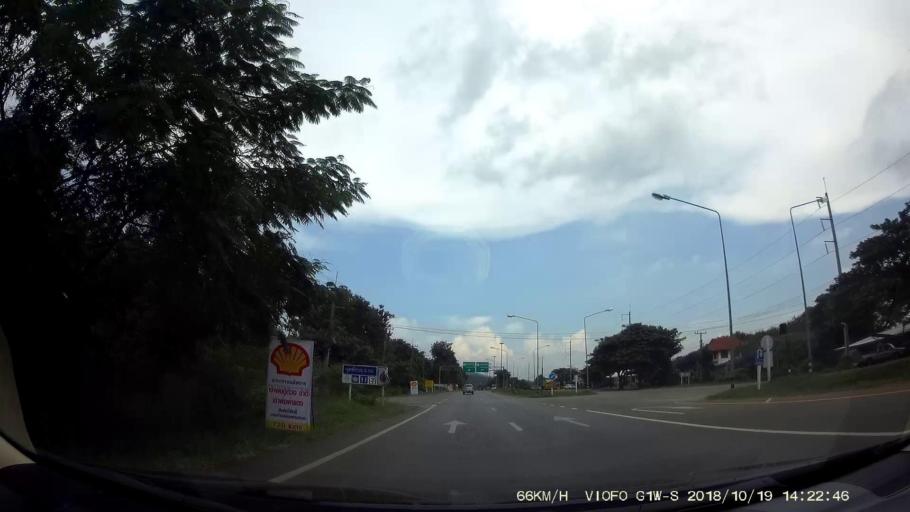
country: TH
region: Chaiyaphum
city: Kaeng Khro
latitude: 16.0658
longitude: 102.2772
